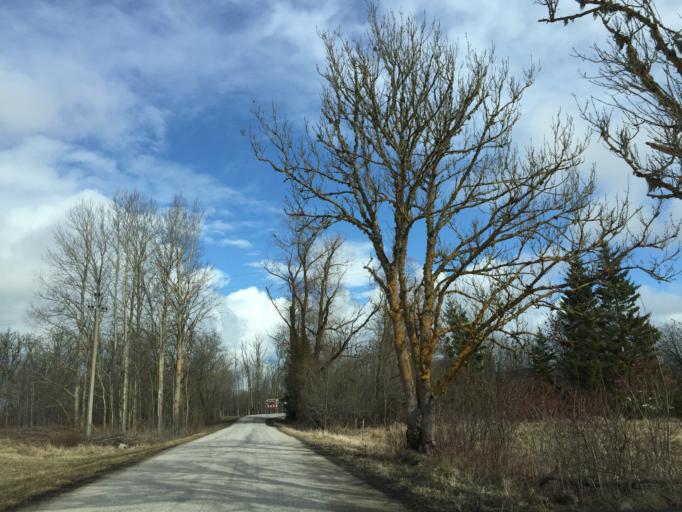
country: EE
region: Laeaene
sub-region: Lihula vald
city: Lihula
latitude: 58.7367
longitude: 23.8317
